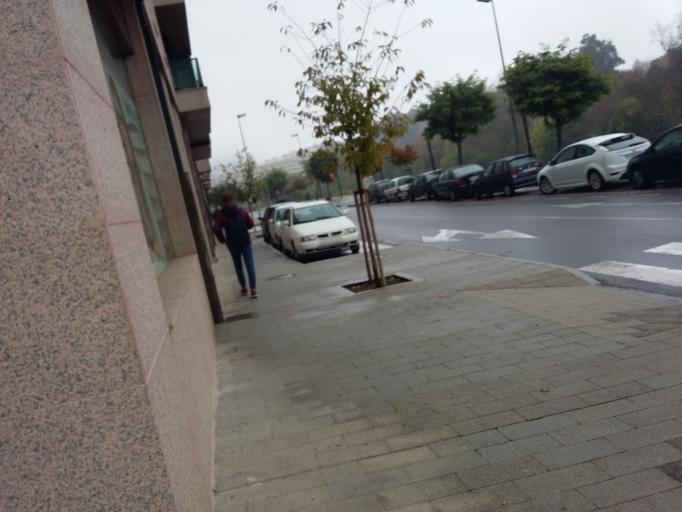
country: ES
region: Galicia
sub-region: Provincia da Coruna
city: Santiago de Compostela
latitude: 42.8679
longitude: -8.5490
